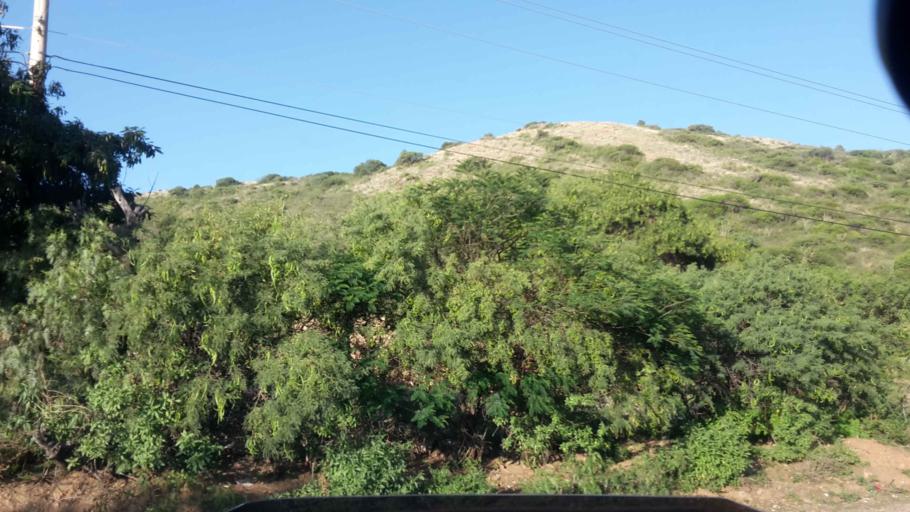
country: BO
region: Cochabamba
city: Tarata
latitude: -17.5275
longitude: -66.0970
